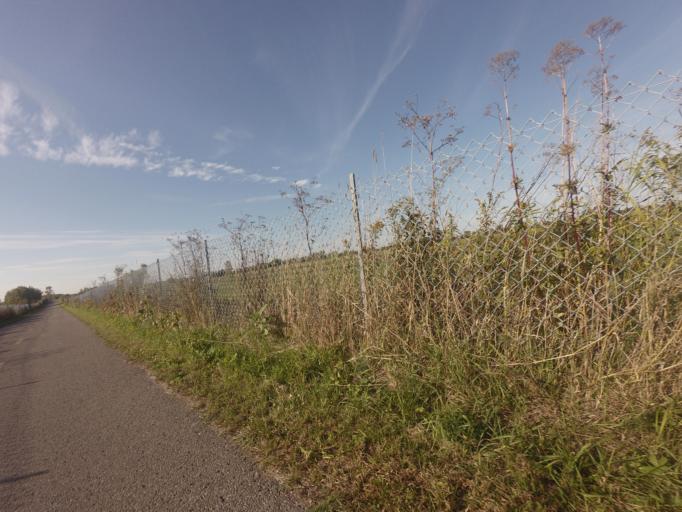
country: CA
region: Quebec
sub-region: Laurentides
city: Saint-Jerome
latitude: 45.7492
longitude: -73.9707
